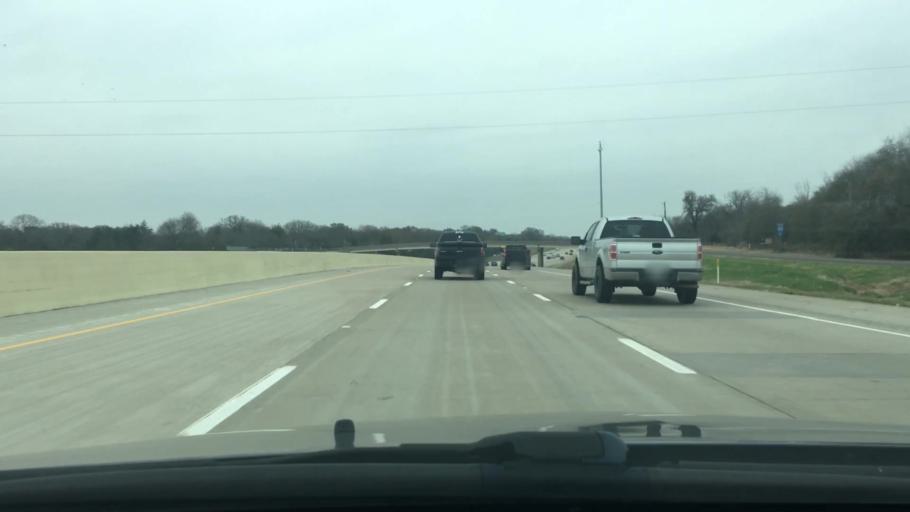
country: US
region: Texas
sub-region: Navarro County
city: Corsicana
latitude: 31.9656
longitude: -96.4210
